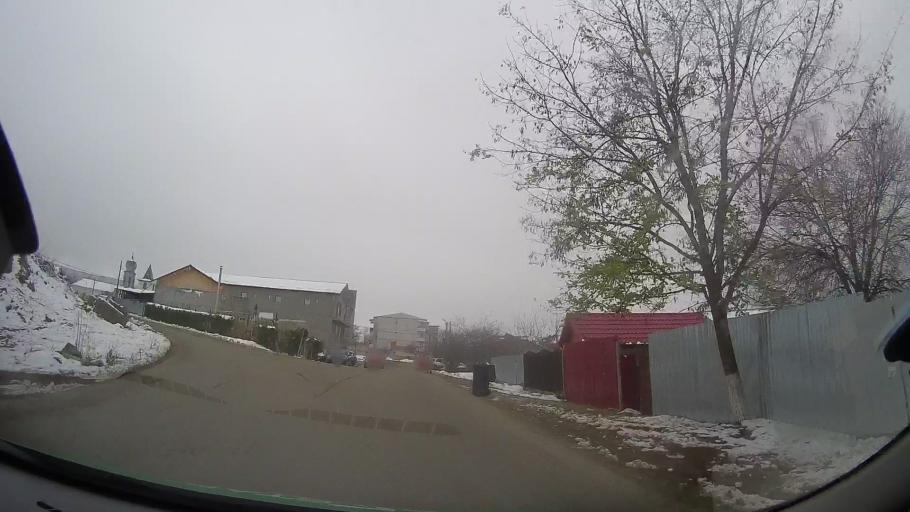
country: RO
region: Bacau
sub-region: Comuna Podu Turcului
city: Podu Turcului
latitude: 46.2045
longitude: 27.3869
